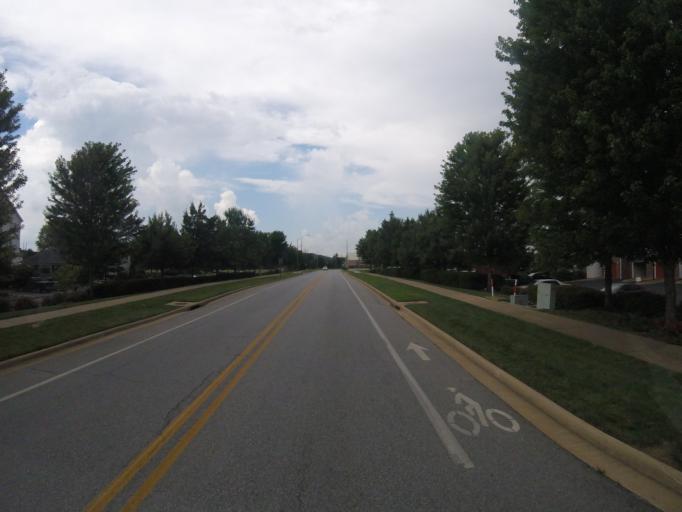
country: US
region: Arkansas
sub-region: Washington County
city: Fayetteville
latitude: 36.0467
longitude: -94.1852
